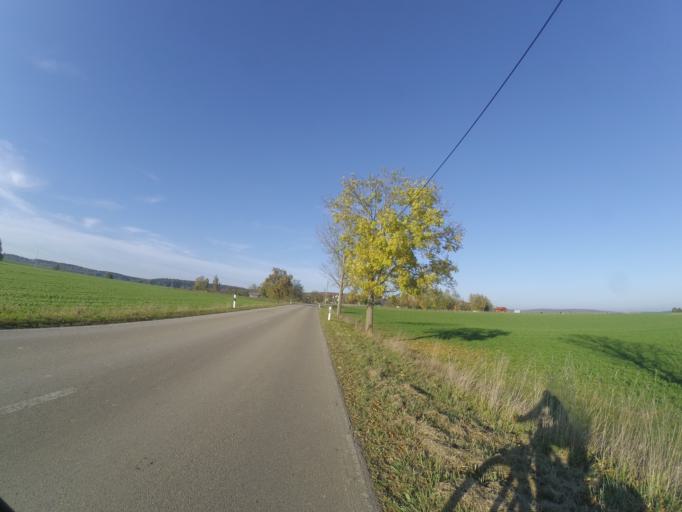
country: DE
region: Baden-Wuerttemberg
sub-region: Tuebingen Region
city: Berghulen
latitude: 48.4676
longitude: 9.7834
